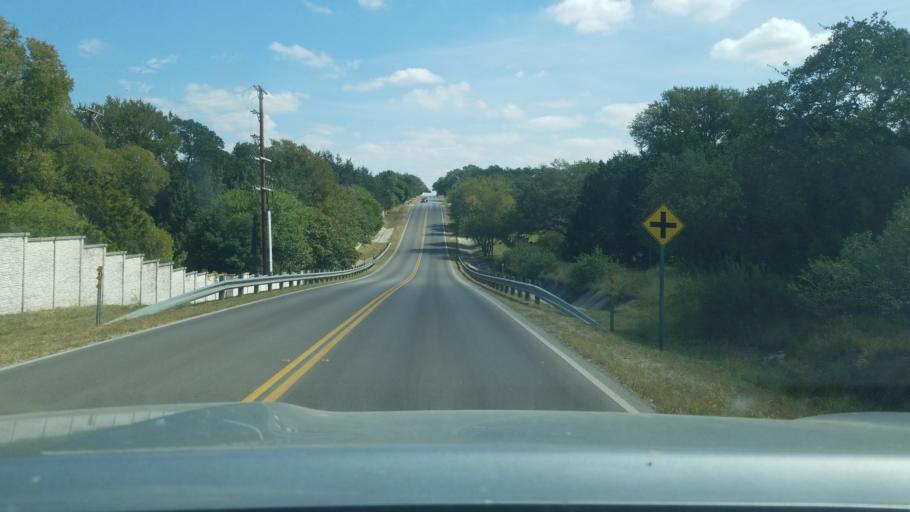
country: US
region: Texas
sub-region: Bexar County
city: Fair Oaks Ranch
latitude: 29.7311
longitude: -98.6452
